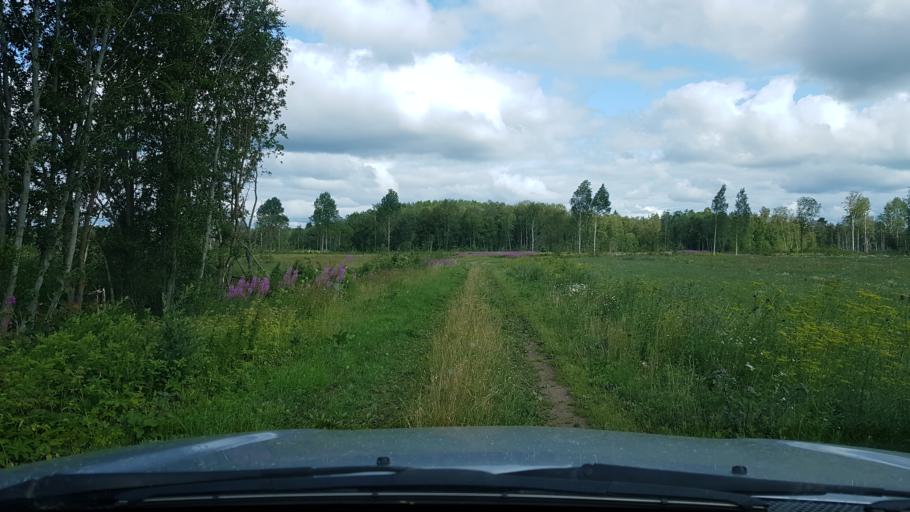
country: EE
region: Ida-Virumaa
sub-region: Narva-Joesuu linn
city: Narva-Joesuu
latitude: 59.3832
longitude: 27.9491
